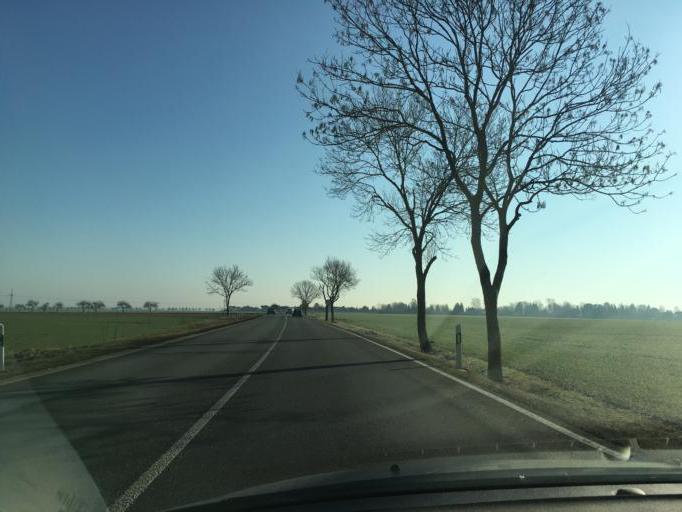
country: DE
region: Saxony
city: Grossposna
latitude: 51.2613
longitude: 12.5149
